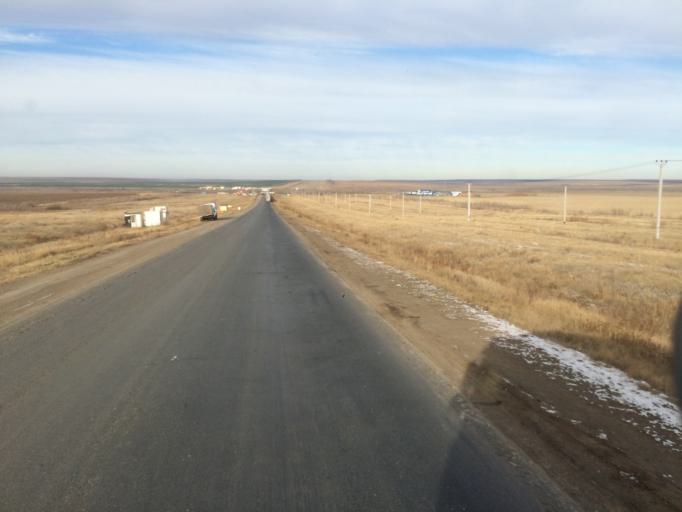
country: KZ
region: Batys Qazaqstan
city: Peremetnoe
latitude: 51.6564
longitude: 51.0094
